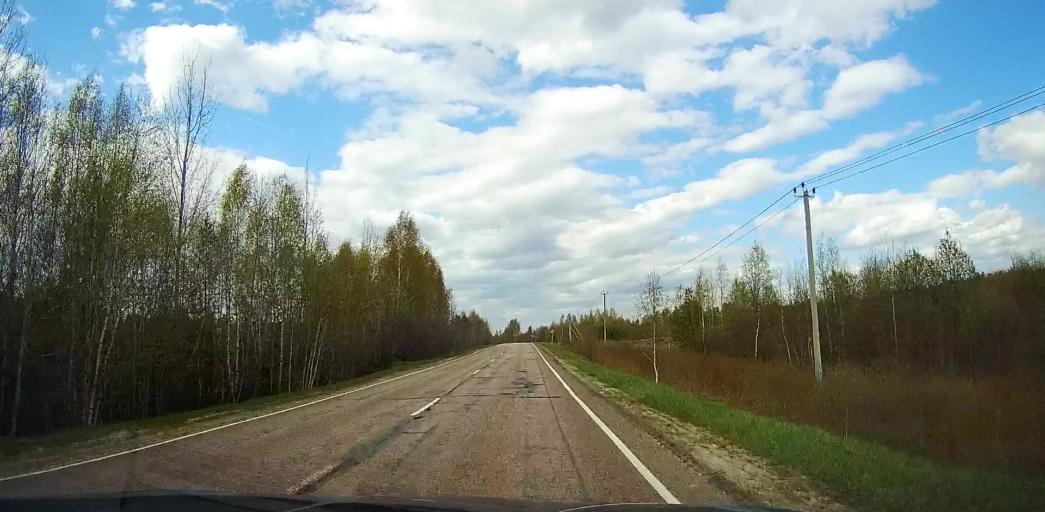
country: RU
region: Moskovskaya
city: Rakhmanovo
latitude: 55.6752
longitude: 38.6452
